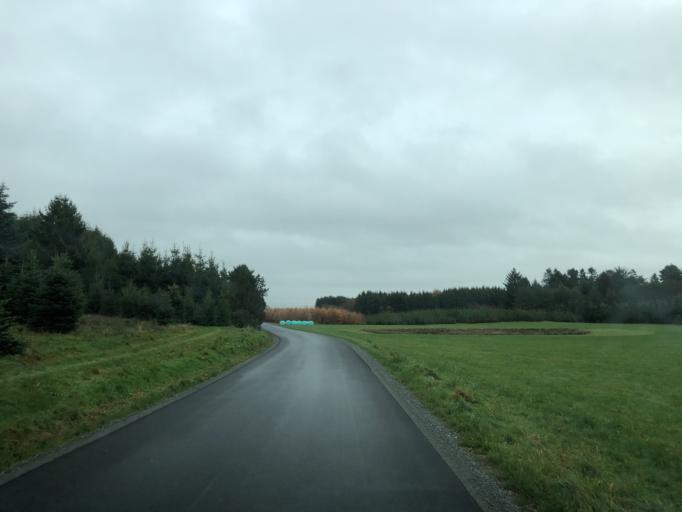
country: DK
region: Central Jutland
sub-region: Silkeborg Kommune
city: Virklund
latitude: 56.0694
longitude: 9.4971
